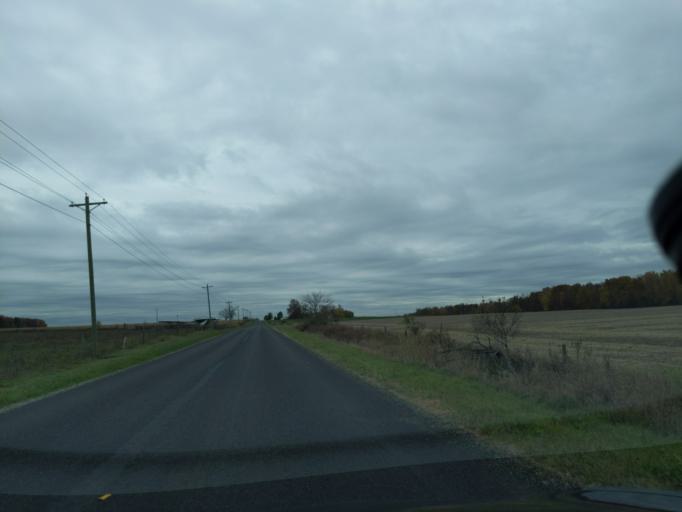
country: US
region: Michigan
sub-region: Eaton County
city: Eaton Rapids
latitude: 42.4576
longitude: -84.6007
